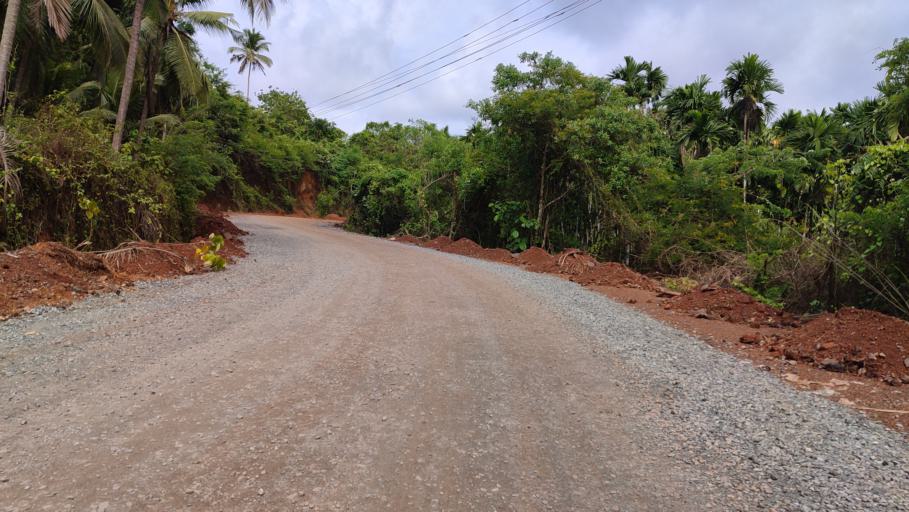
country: IN
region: Kerala
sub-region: Kasaragod District
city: Kasaragod
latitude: 12.5158
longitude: 75.0715
